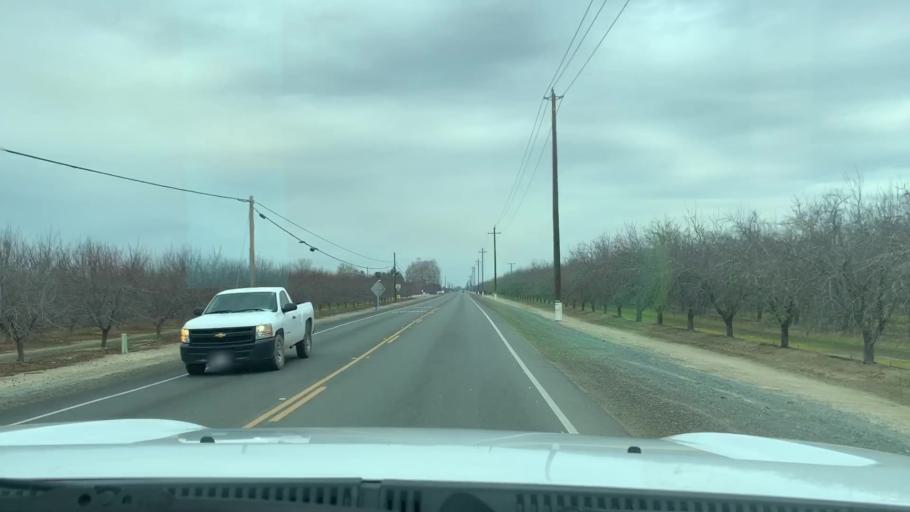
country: US
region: California
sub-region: Kern County
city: Shafter
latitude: 35.3995
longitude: -119.2520
